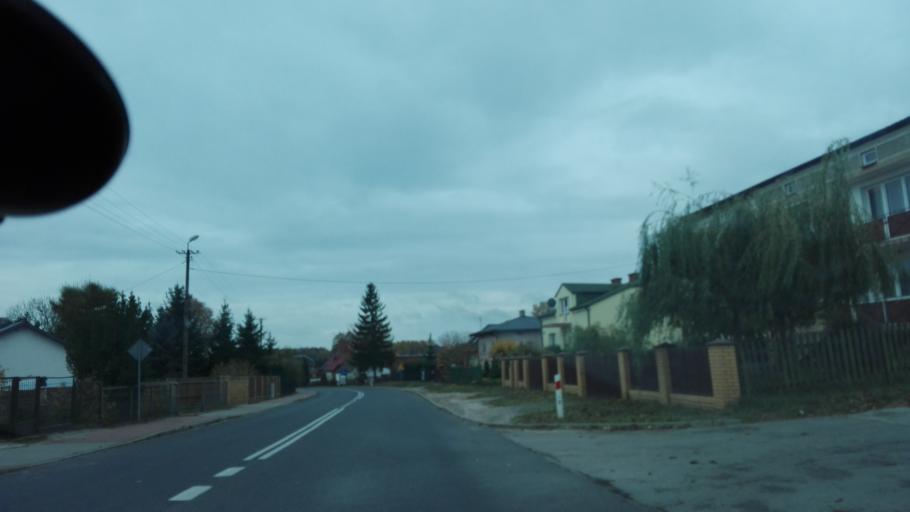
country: PL
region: Lublin Voivodeship
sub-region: Powiat pulawski
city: Pulawy
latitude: 51.4349
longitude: 21.9122
